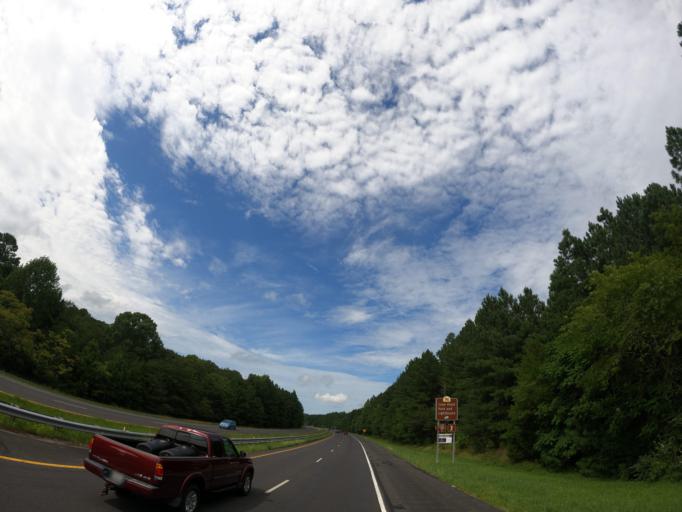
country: US
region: Maryland
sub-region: Calvert County
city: Lusby
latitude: 38.3834
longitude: -76.4371
